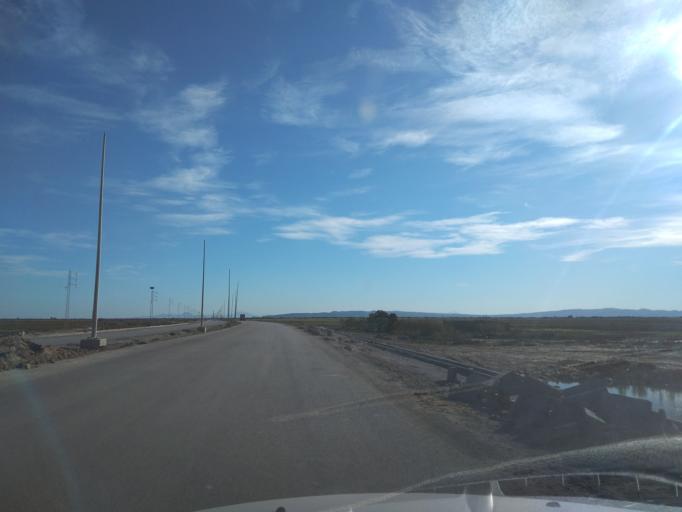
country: TN
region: Ariana
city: Qal'at al Andalus
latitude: 37.0378
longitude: 10.1327
